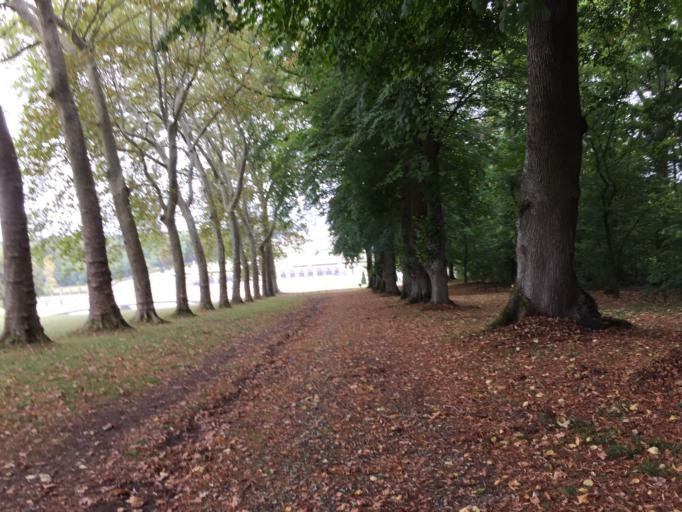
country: FR
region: Ile-de-France
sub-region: Departement de Seine-et-Marne
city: Maincy
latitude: 48.5577
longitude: 2.7161
